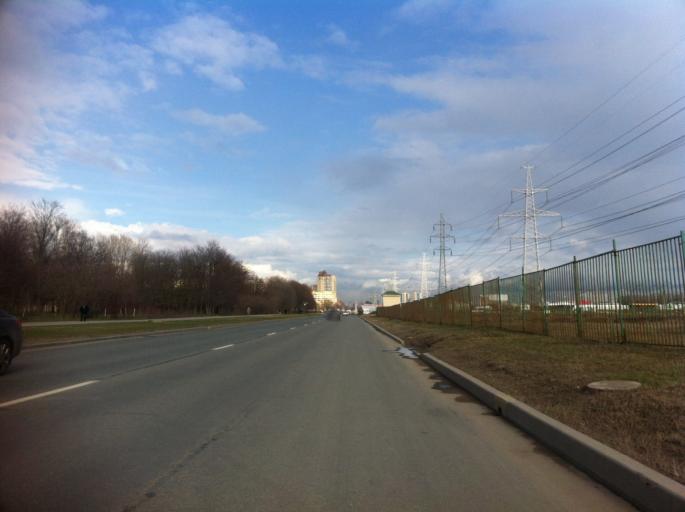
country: RU
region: St.-Petersburg
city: Uritsk
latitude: 59.8474
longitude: 30.1624
